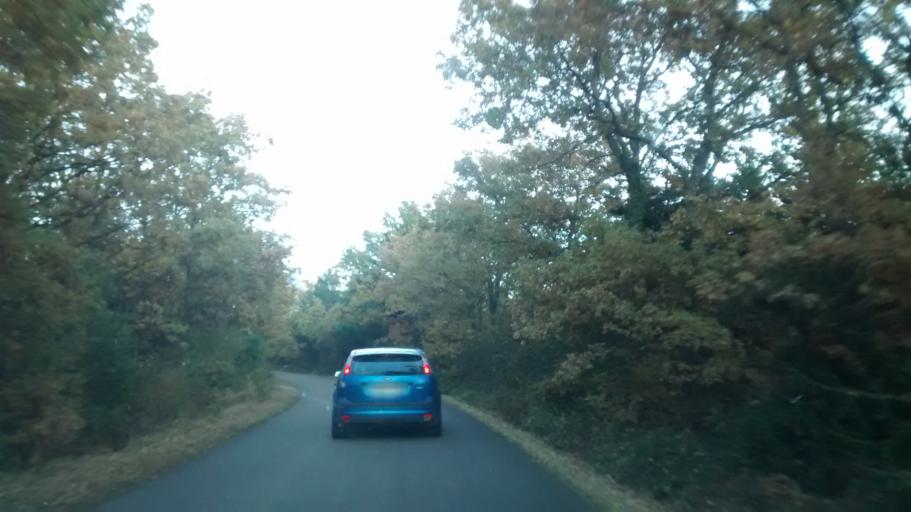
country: ES
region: Aragon
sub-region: Provincia de Zaragoza
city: Litago
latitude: 41.7890
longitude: -1.7696
